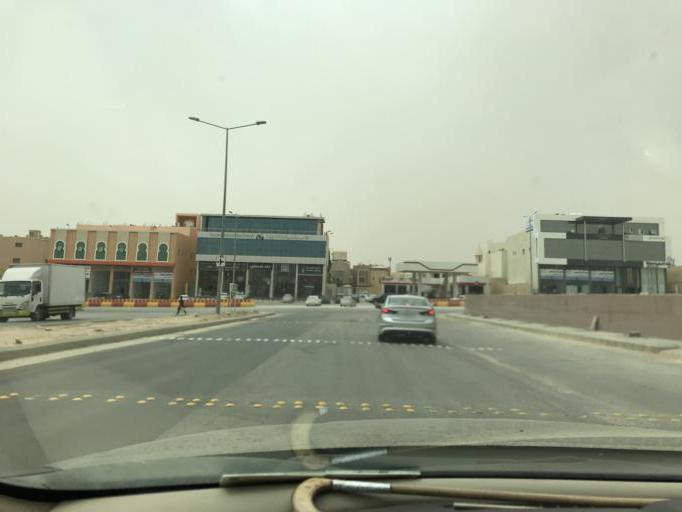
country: SA
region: Ar Riyad
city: Riyadh
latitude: 24.8104
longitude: 46.6014
